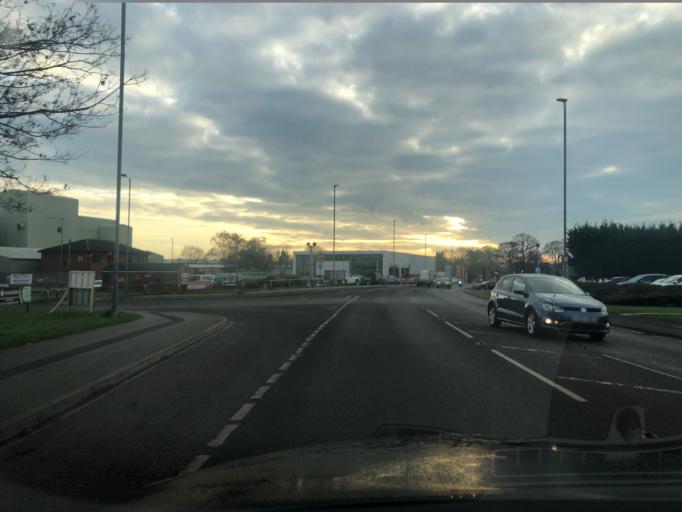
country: GB
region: England
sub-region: North Yorkshire
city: Northallerton
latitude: 54.3483
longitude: -1.4422
